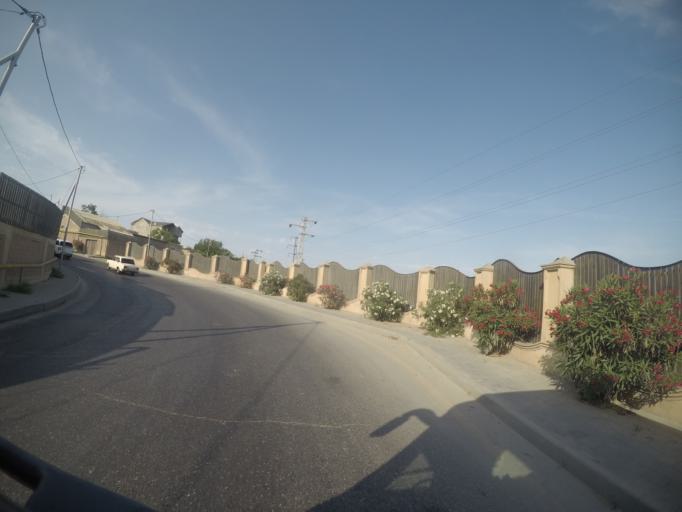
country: AZ
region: Baki
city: Binagadi
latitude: 40.4641
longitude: 49.8422
